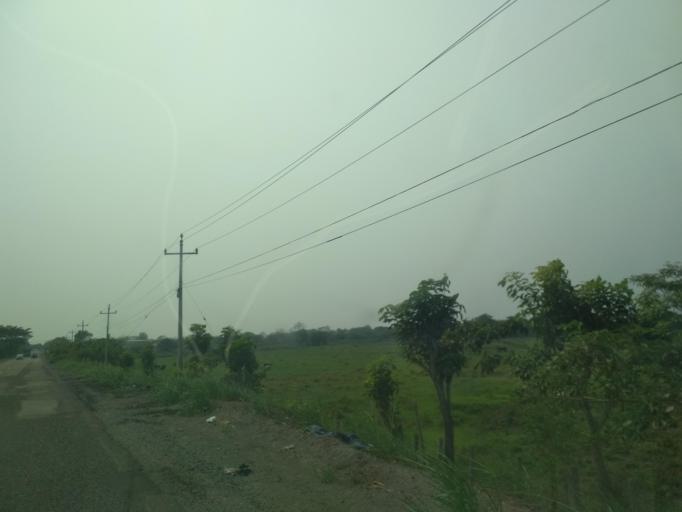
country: MX
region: Veracruz
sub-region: Veracruz
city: Delfino Victoria (Santa Fe)
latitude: 19.2003
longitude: -96.3049
